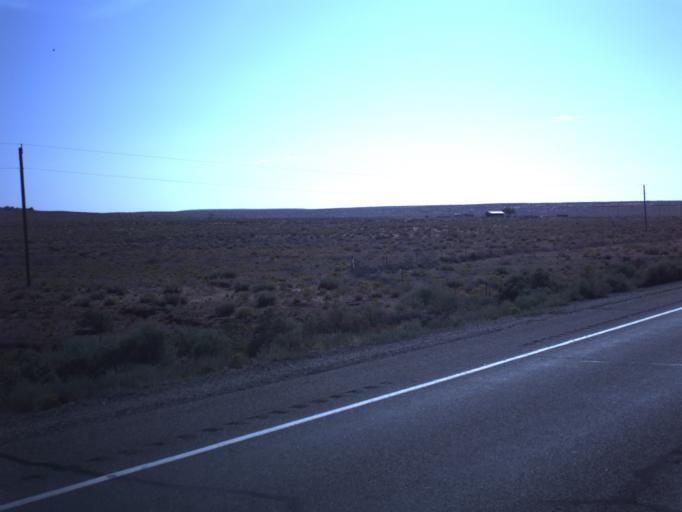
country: US
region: Utah
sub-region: San Juan County
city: Blanding
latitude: 37.1770
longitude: -109.5852
